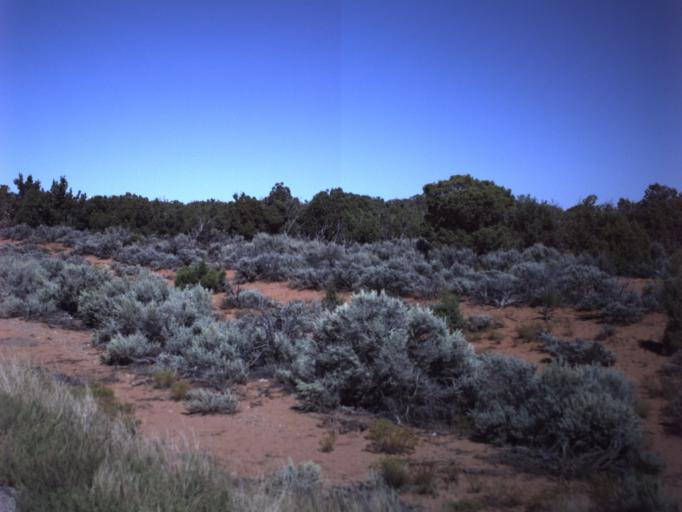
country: US
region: Utah
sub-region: San Juan County
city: Blanding
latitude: 37.2900
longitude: -109.9382
